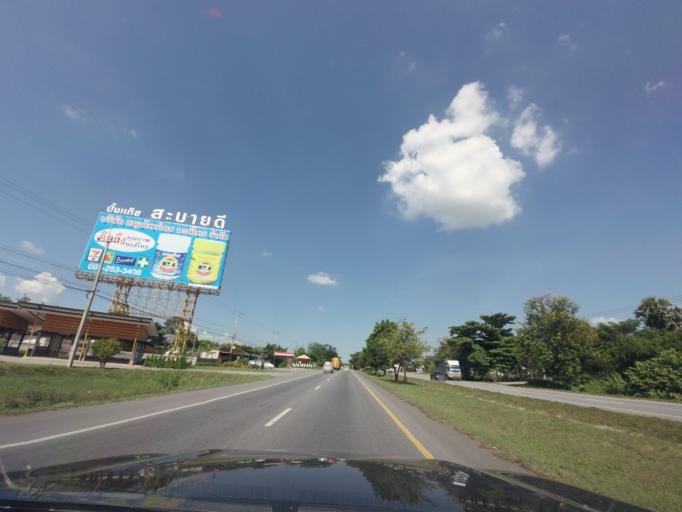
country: TH
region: Nakhon Ratchasima
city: Non Sung
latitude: 15.1431
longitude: 102.3188
